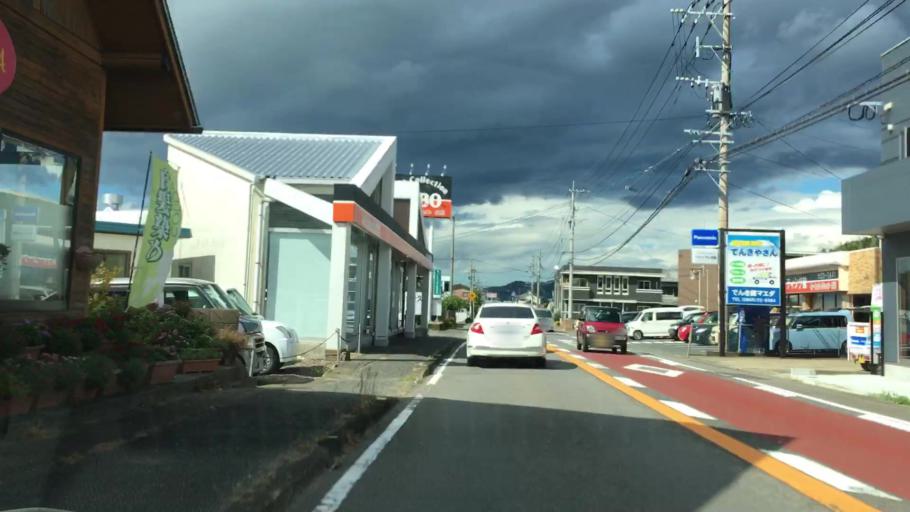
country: JP
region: Saga Prefecture
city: Imaricho-ko
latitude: 33.2488
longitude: 129.8524
